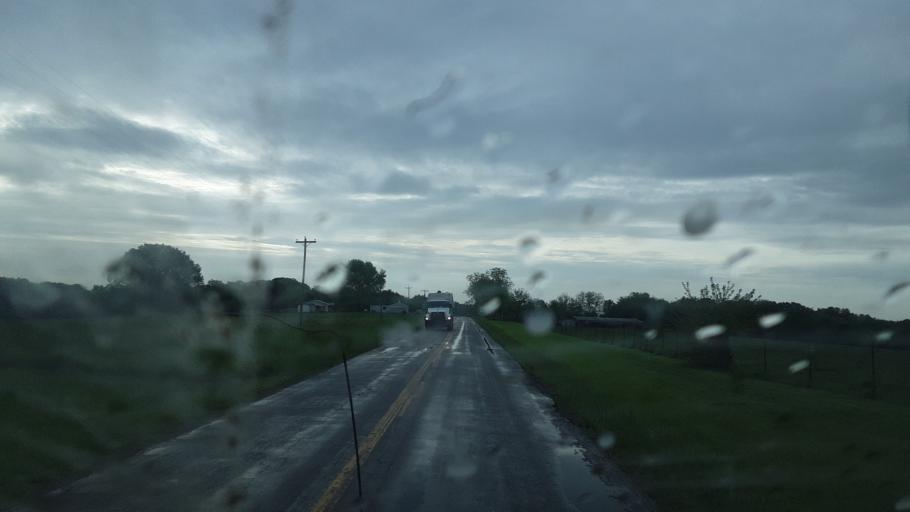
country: US
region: Missouri
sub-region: Clark County
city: Kahoka
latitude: 40.4386
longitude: -91.5989
